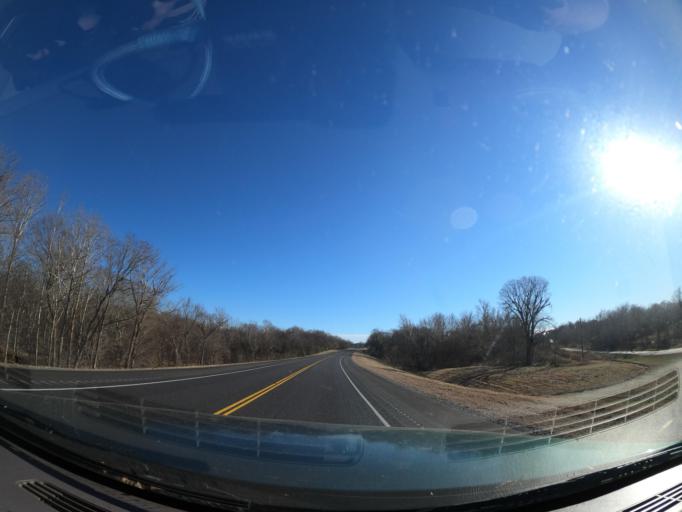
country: US
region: Oklahoma
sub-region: McIntosh County
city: Eufaula
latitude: 35.2658
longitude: -95.5818
